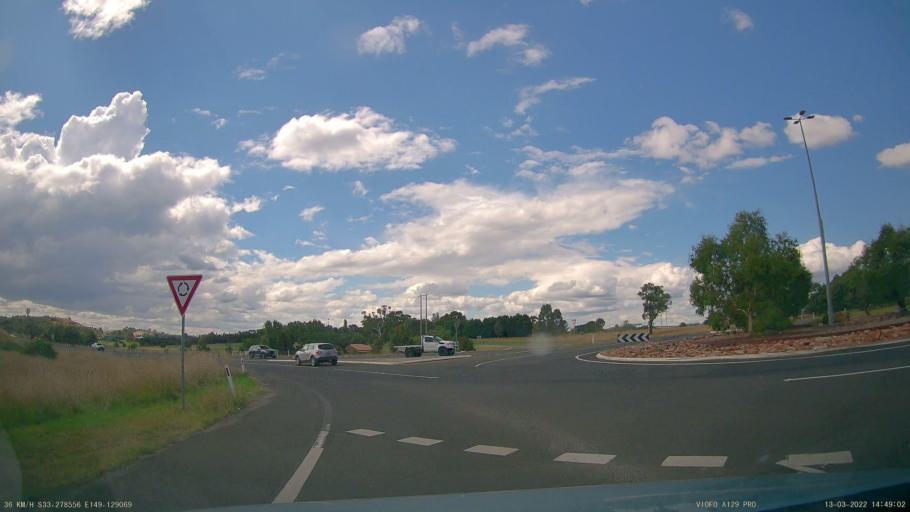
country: AU
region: New South Wales
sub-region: Orange Municipality
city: Orange
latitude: -33.2786
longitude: 149.1293
